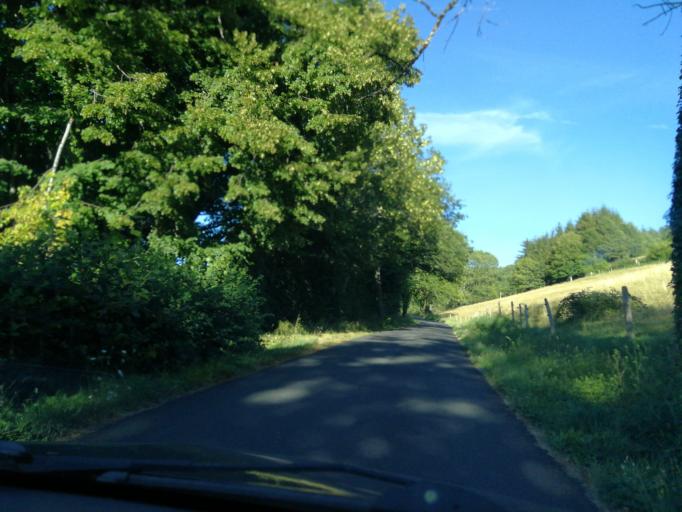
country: FR
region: Auvergne
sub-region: Departement du Cantal
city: Vic-sur-Cere
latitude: 45.0953
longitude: 2.5632
